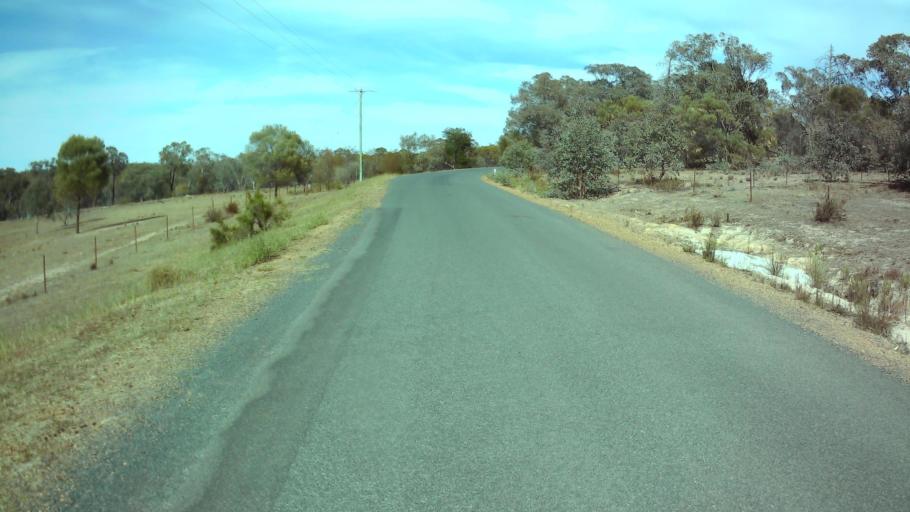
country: AU
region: New South Wales
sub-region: Weddin
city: Grenfell
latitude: -33.8791
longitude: 148.1958
